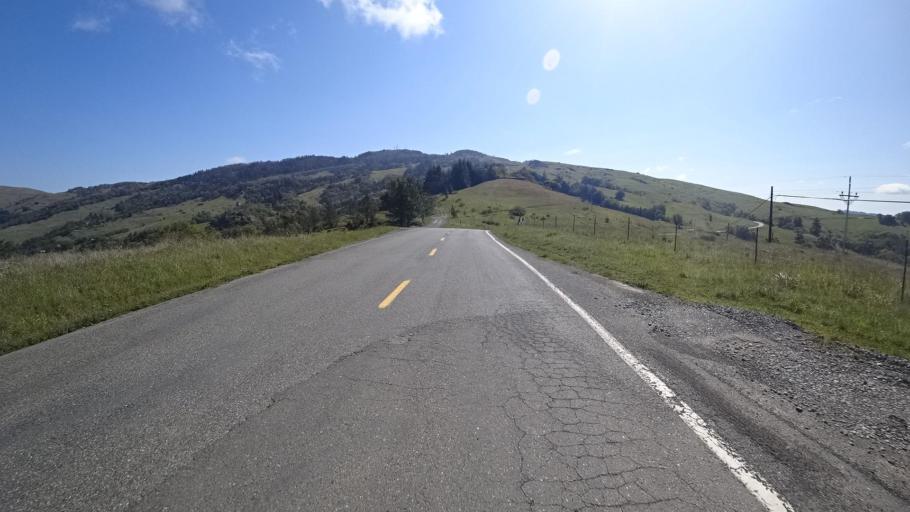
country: US
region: California
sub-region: Humboldt County
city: Redway
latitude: 40.1122
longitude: -123.7231
